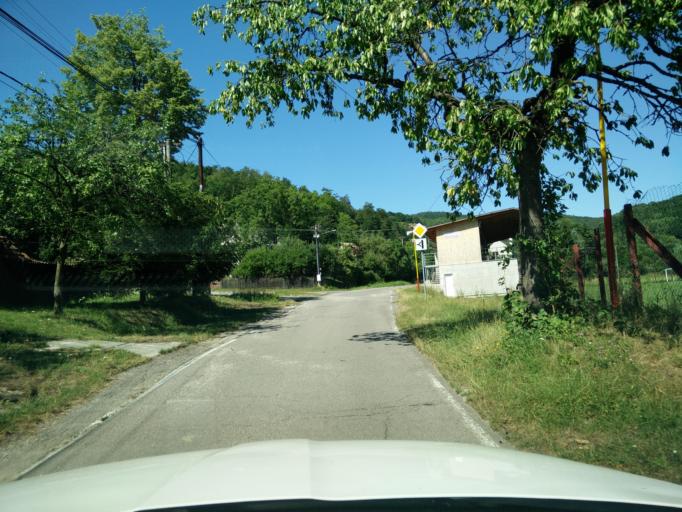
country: SK
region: Nitriansky
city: Prievidza
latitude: 48.8039
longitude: 18.7049
